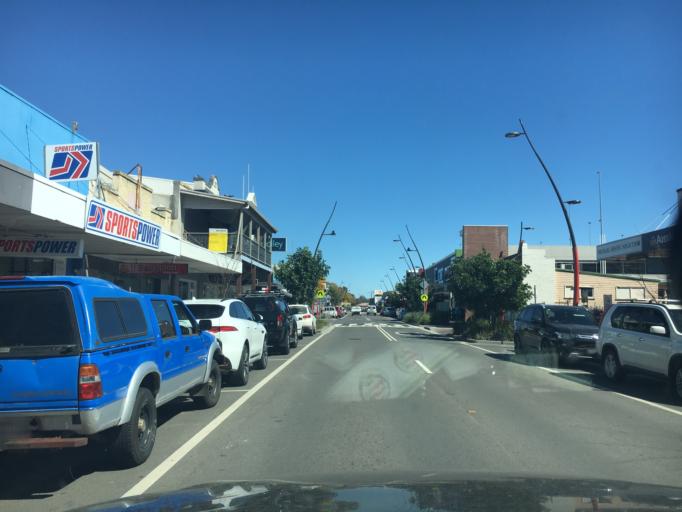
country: AU
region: New South Wales
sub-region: Singleton
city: Singleton
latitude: -32.5661
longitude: 151.1664
